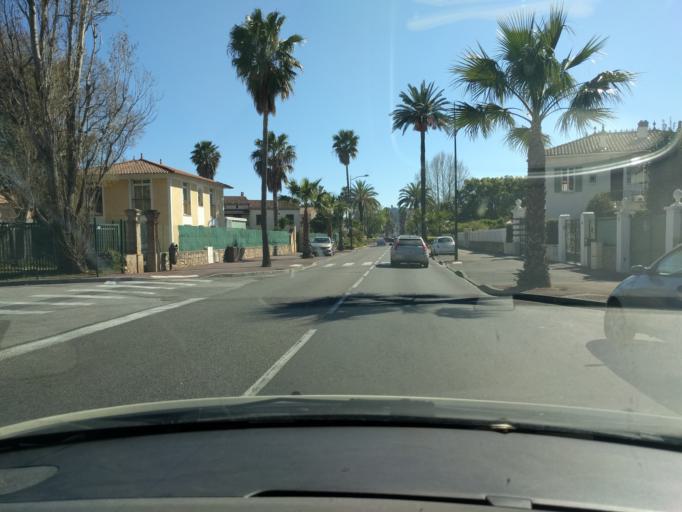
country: FR
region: Provence-Alpes-Cote d'Azur
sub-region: Departement du Var
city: Hyeres
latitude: 43.1147
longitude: 6.1232
